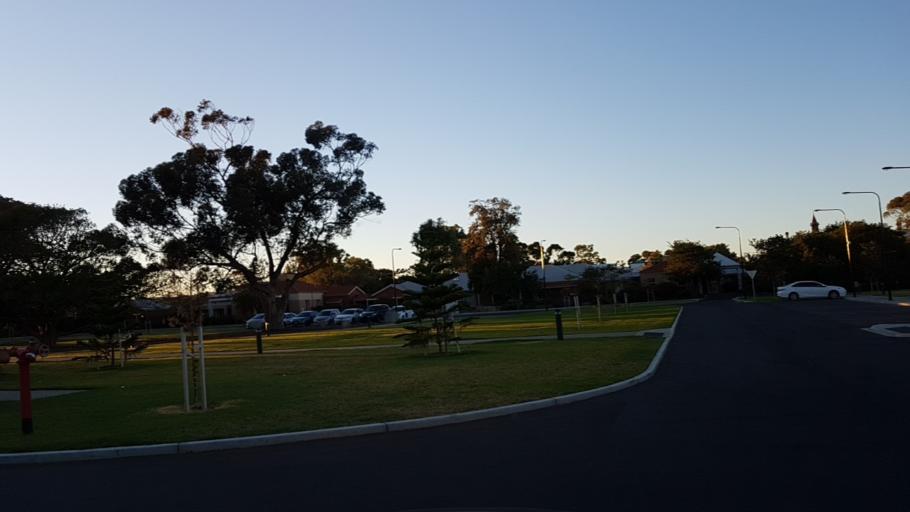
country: AU
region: South Australia
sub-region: Holdfast Bay
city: North Brighton
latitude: -35.0045
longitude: 138.5154
